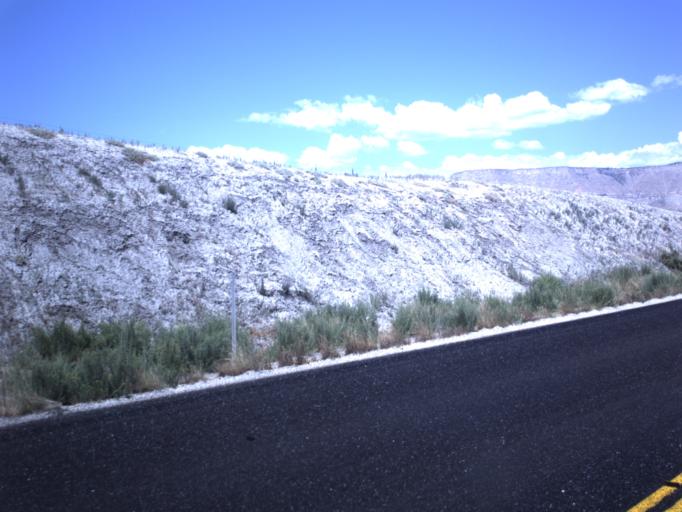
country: US
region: Utah
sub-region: Emery County
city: Ferron
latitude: 39.0628
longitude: -111.1308
